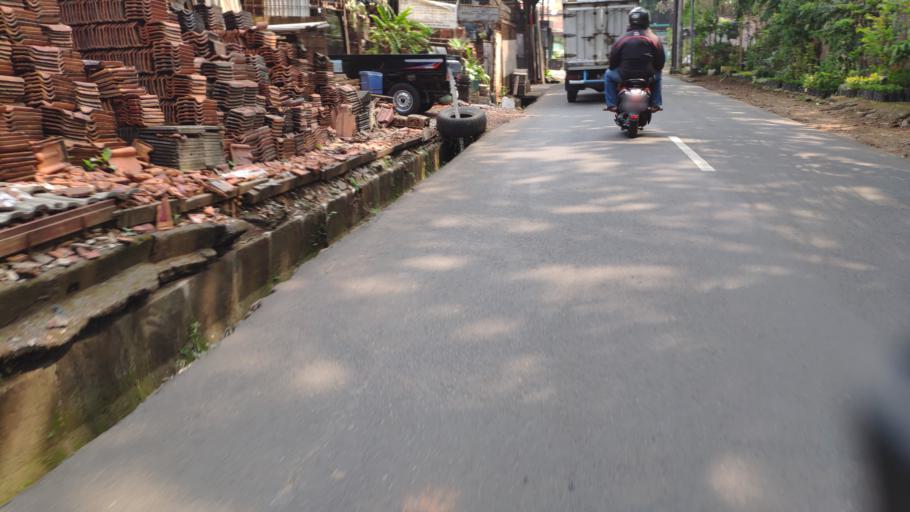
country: ID
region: West Java
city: Depok
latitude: -6.3108
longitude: 106.8268
